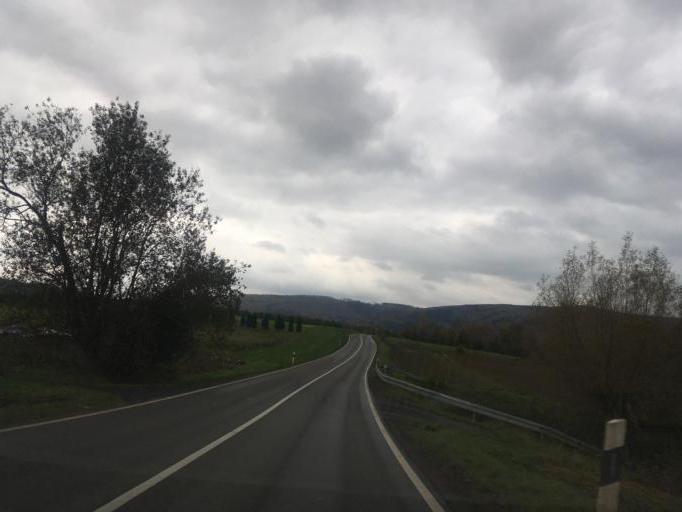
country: DE
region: Lower Saxony
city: Bodenfelde
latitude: 51.6149
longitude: 9.5504
